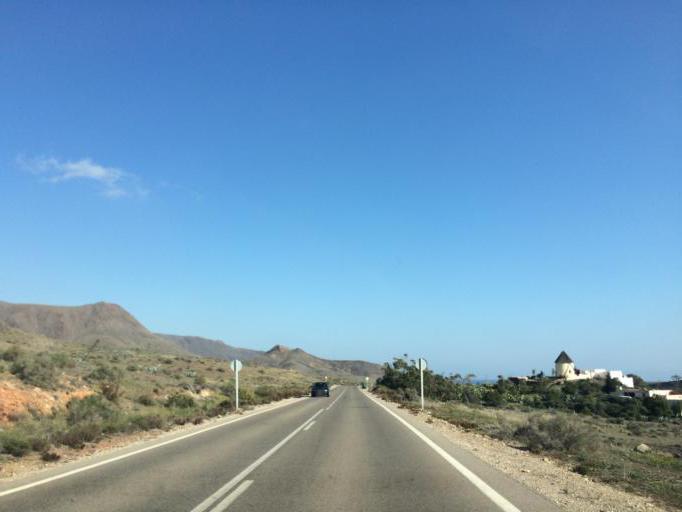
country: ES
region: Andalusia
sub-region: Provincia de Almeria
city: San Jose
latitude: 36.7990
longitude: -2.0995
